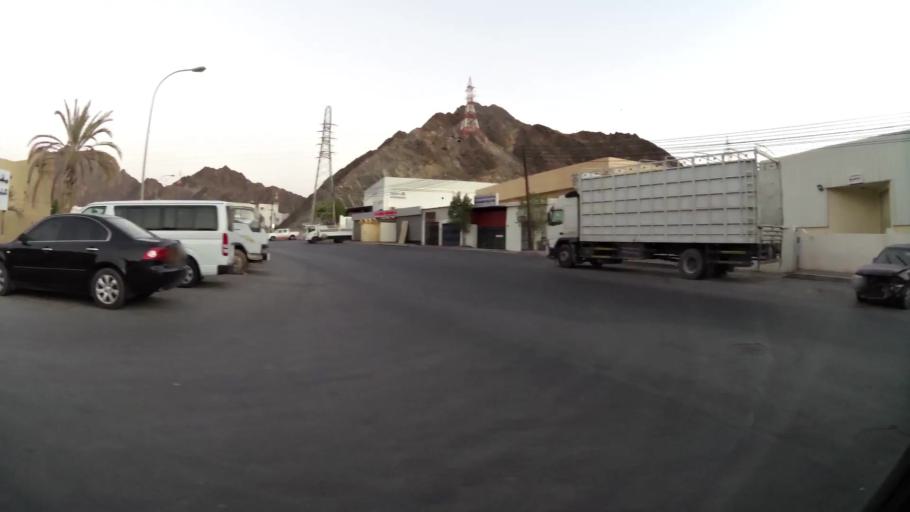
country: OM
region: Muhafazat Masqat
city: Muscat
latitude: 23.5920
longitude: 58.5667
